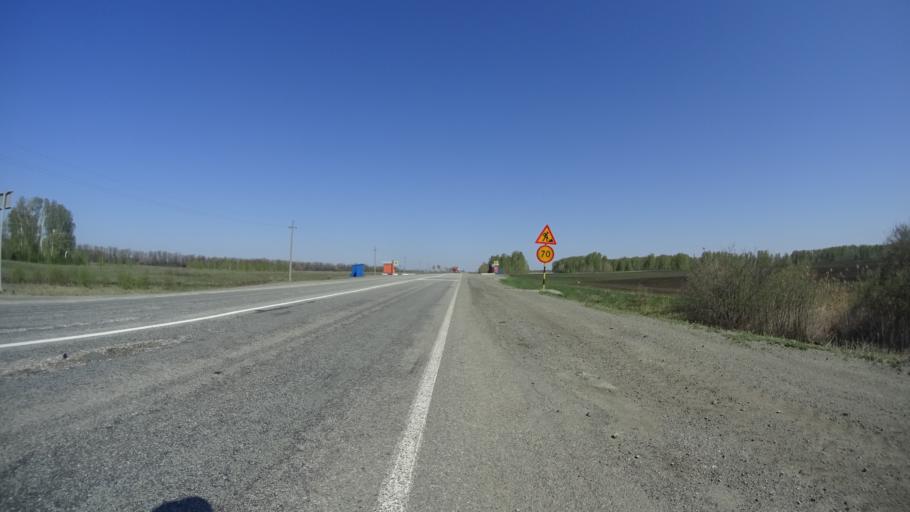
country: RU
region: Chelyabinsk
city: Troitsk
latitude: 54.1872
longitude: 61.4340
